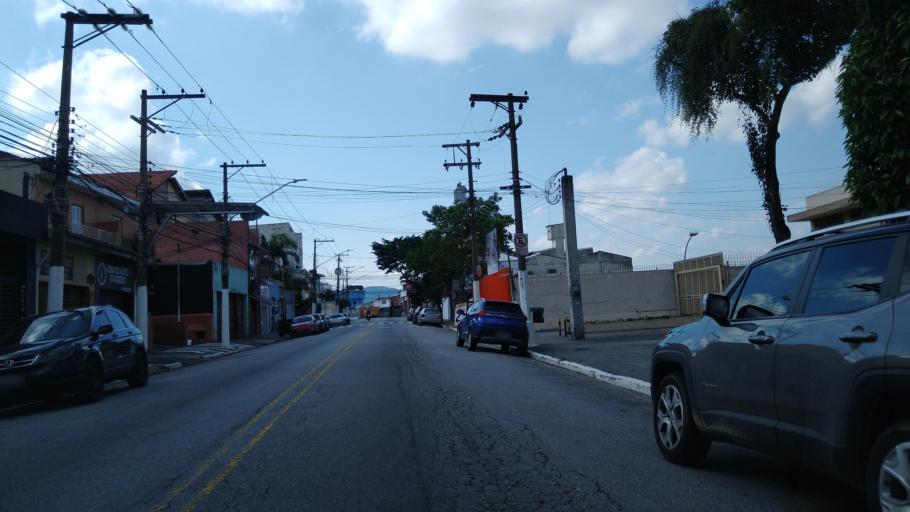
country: BR
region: Sao Paulo
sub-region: Sao Paulo
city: Sao Paulo
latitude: -23.4977
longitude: -46.6421
